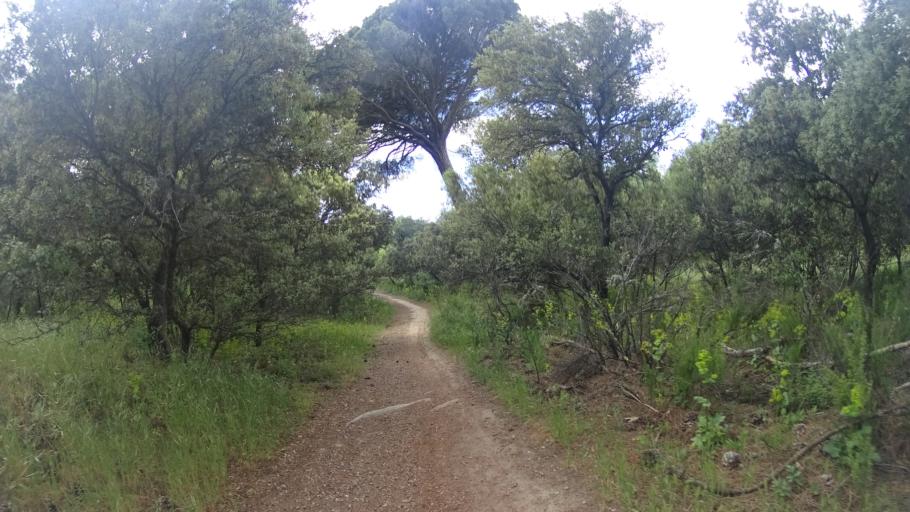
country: ES
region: Madrid
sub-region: Provincia de Madrid
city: Brunete
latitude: 40.3969
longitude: -3.9432
